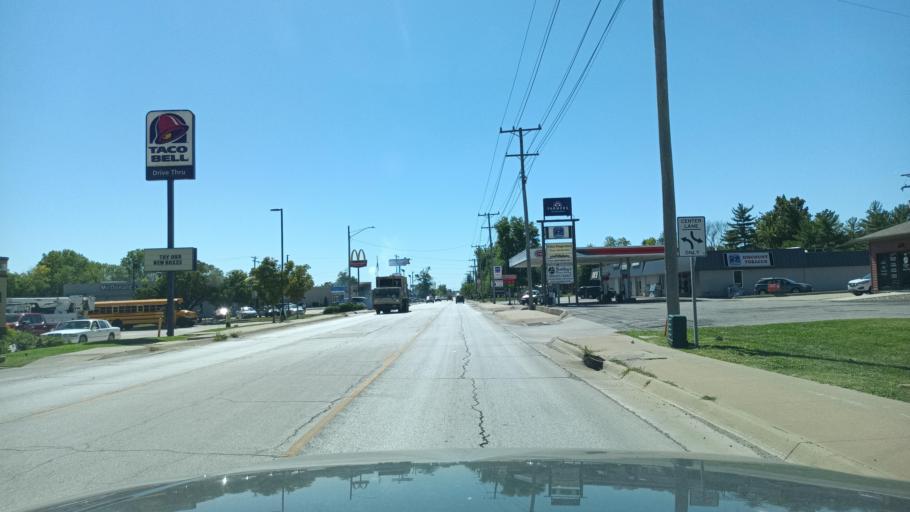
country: US
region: Missouri
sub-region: Adair County
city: Kirksville
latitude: 40.1856
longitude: -92.5720
